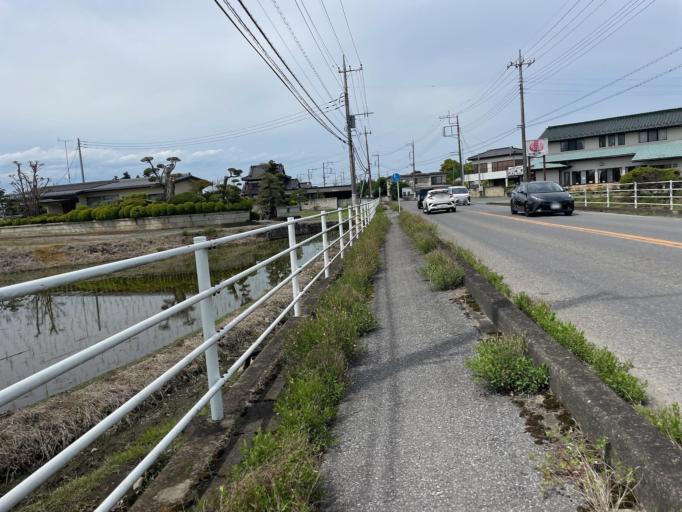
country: JP
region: Tochigi
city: Mibu
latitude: 36.4707
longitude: 139.7647
